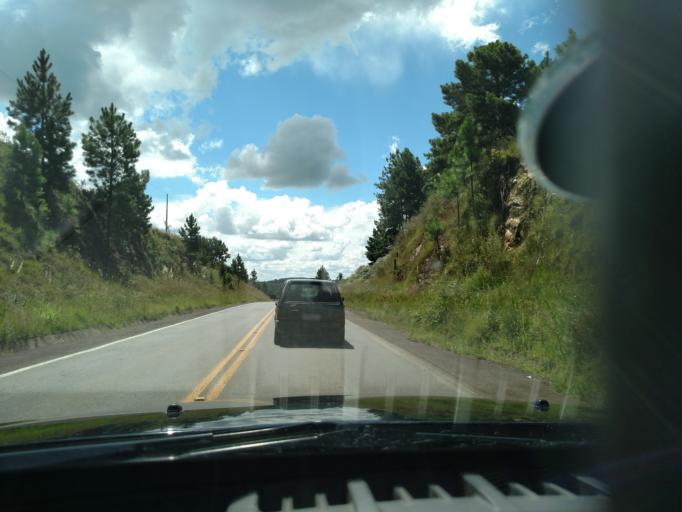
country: BR
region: Santa Catarina
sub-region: Lages
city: Lages
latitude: -27.8469
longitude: -50.2268
